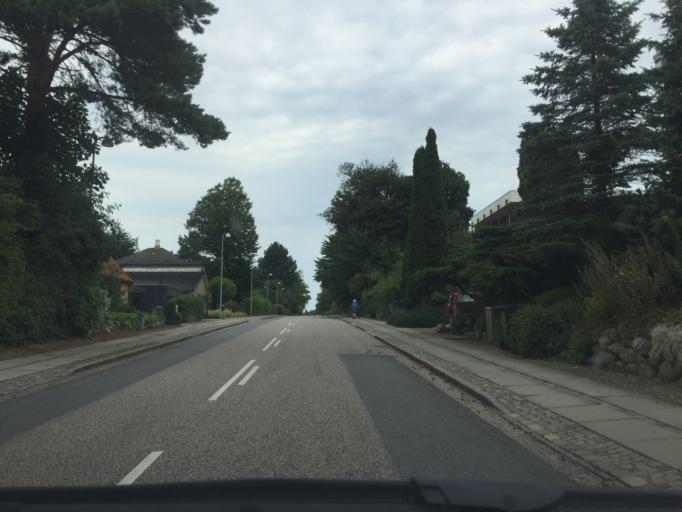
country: DK
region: Capital Region
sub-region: Lyngby-Tarbaek Kommune
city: Kongens Lyngby
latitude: 55.7799
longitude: 12.5028
